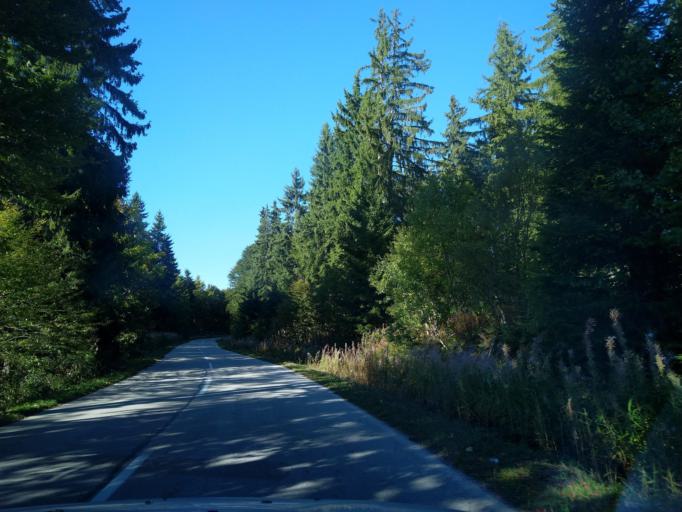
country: RS
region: Central Serbia
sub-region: Moravicki Okrug
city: Ivanjica
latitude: 43.4128
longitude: 20.2658
